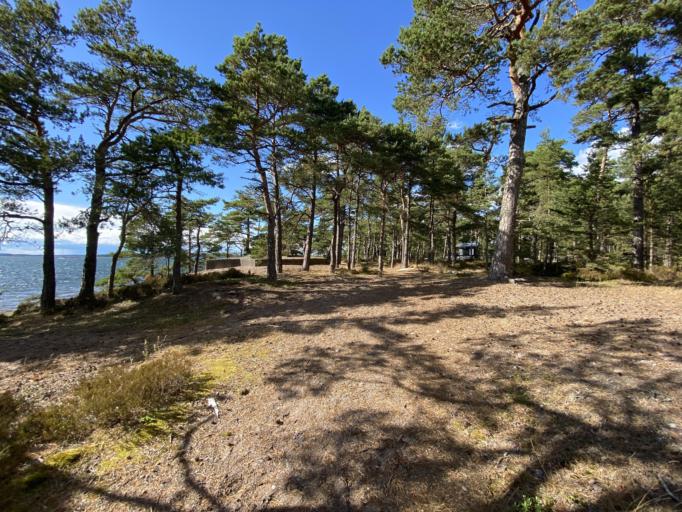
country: SE
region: Stockholm
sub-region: Varmdo Kommun
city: Holo
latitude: 59.2801
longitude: 18.9023
